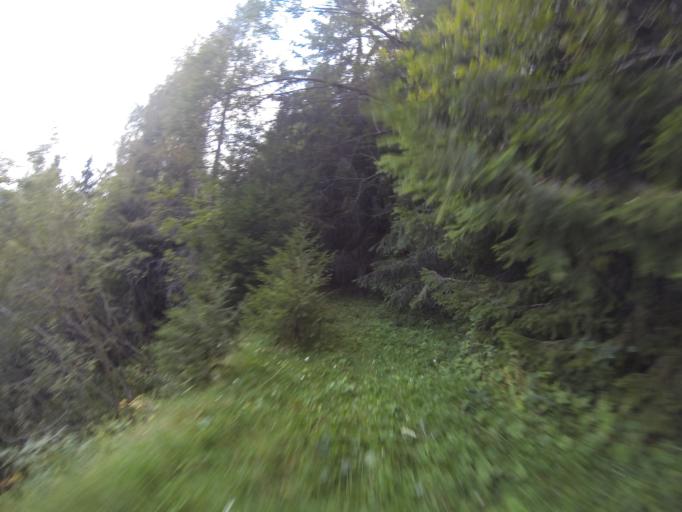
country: RO
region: Gorj
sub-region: Comuna Polovragi
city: Polovragi
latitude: 45.2738
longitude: 23.8280
